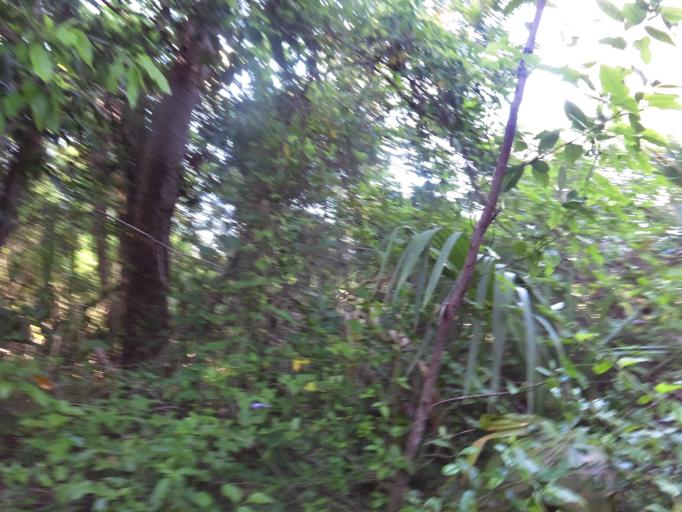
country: US
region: Florida
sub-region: Duval County
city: Atlantic Beach
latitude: 30.3831
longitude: -81.4849
